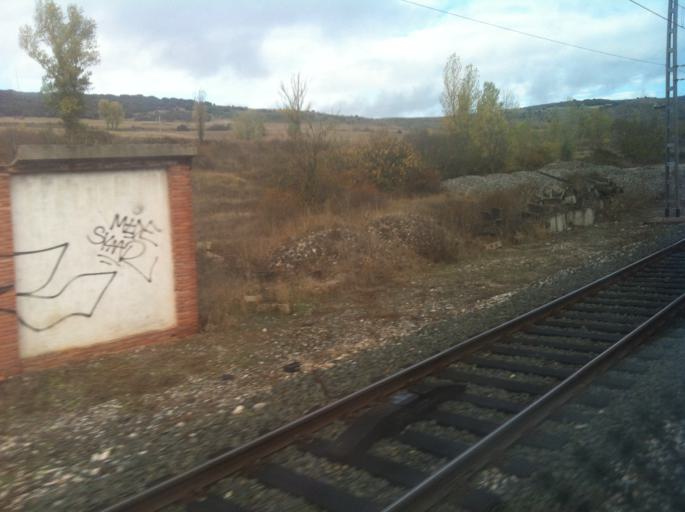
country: ES
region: Castille and Leon
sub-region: Provincia de Burgos
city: Santa Olalla de Bureba
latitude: 42.4640
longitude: -3.4475
